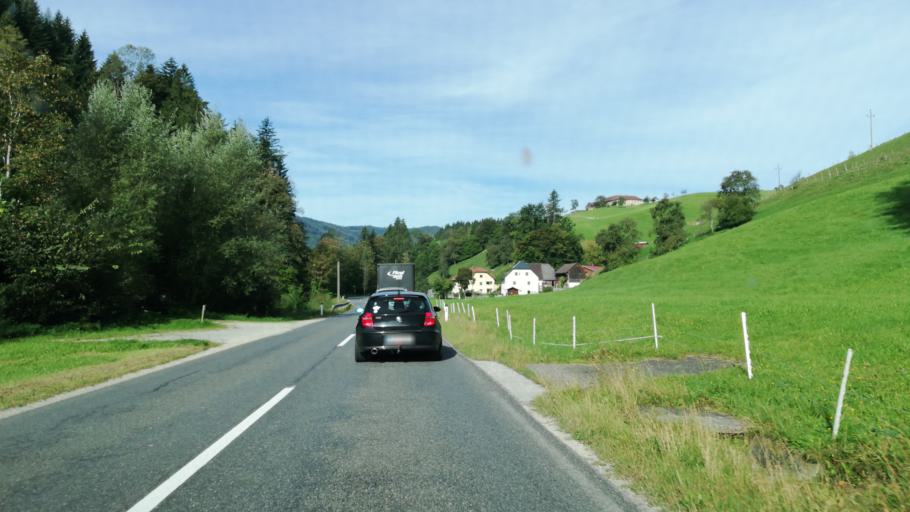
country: AT
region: Lower Austria
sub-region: Politischer Bezirk Amstetten
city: Behamberg
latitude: 47.9918
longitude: 14.5251
